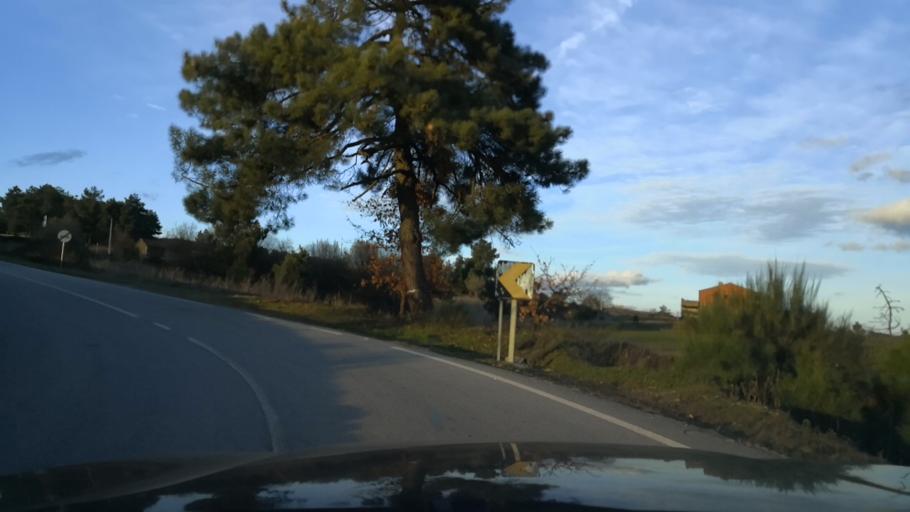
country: PT
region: Braganca
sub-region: Carrazeda de Ansiaes
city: Carrazeda de Anciaes
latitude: 41.2281
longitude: -7.3052
